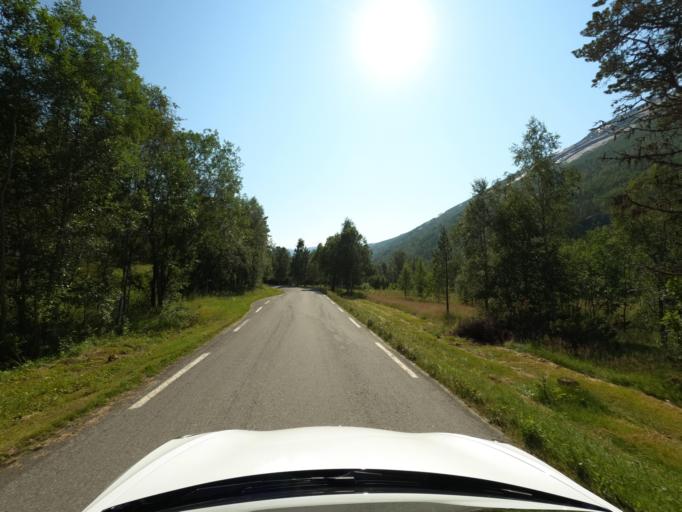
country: NO
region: Nordland
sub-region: Narvik
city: Narvik
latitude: 68.1892
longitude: 17.5519
